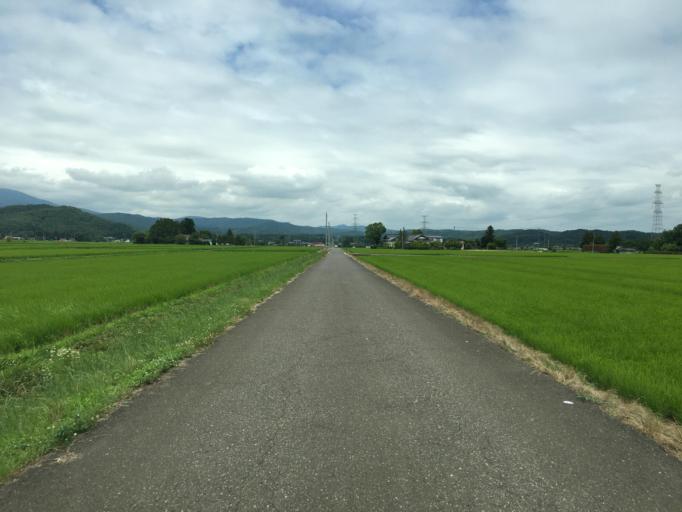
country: JP
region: Fukushima
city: Motomiya
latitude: 37.5485
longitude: 140.3890
